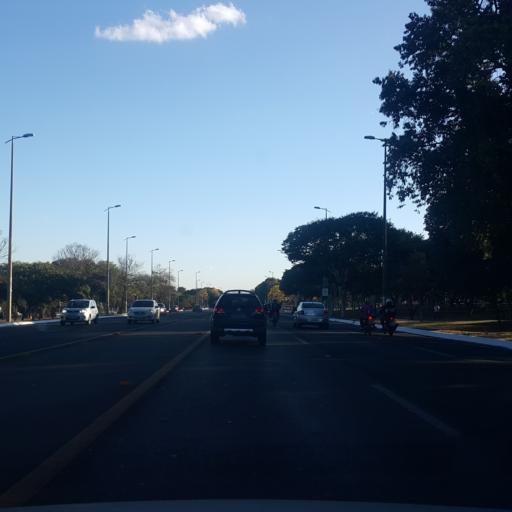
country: BR
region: Federal District
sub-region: Brasilia
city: Brasilia
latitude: -15.8273
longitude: -47.9151
